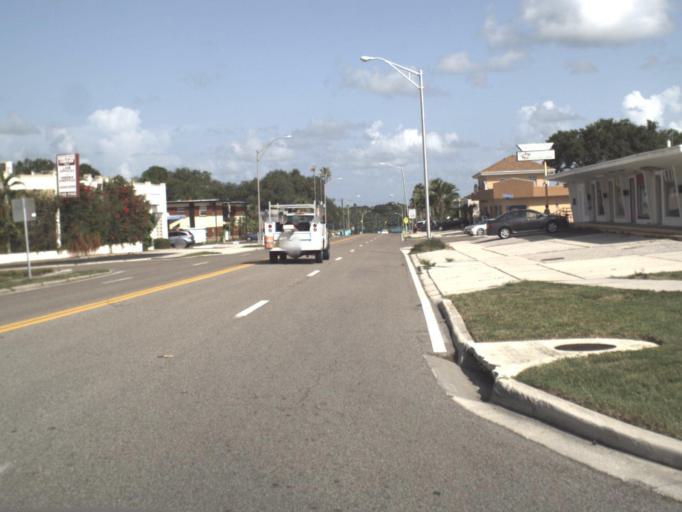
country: US
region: Florida
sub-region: Pinellas County
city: Clearwater
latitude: 27.9625
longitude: -82.7769
